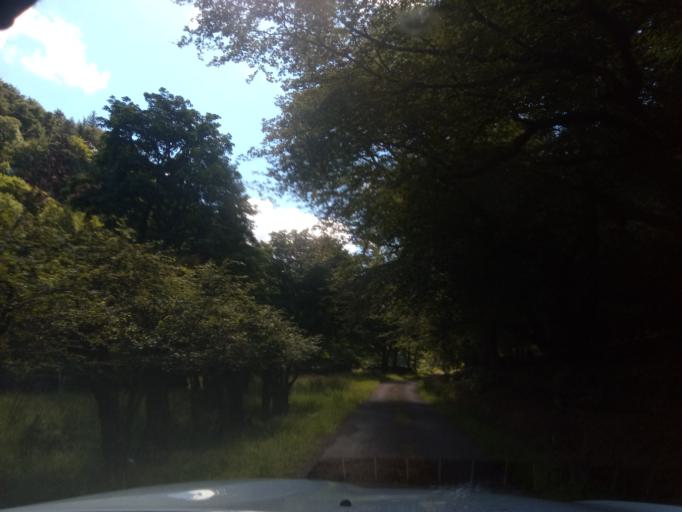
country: GB
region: Scotland
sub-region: Argyll and Bute
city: Isle Of Mull
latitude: 56.7791
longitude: -5.8252
